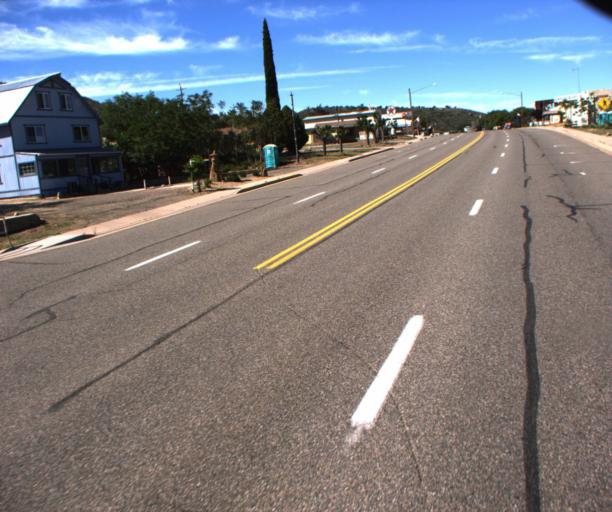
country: US
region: Arizona
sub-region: Yavapai County
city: Congress
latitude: 34.2240
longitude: -112.7456
